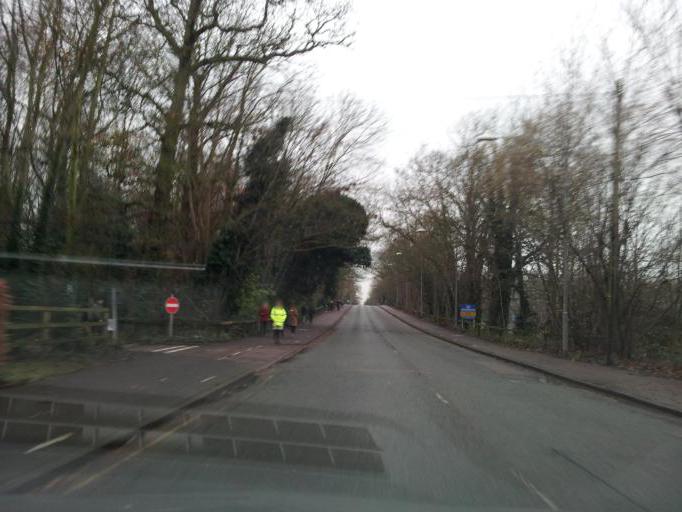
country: GB
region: England
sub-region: Cambridgeshire
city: Cambridge
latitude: 52.1794
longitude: 0.1335
